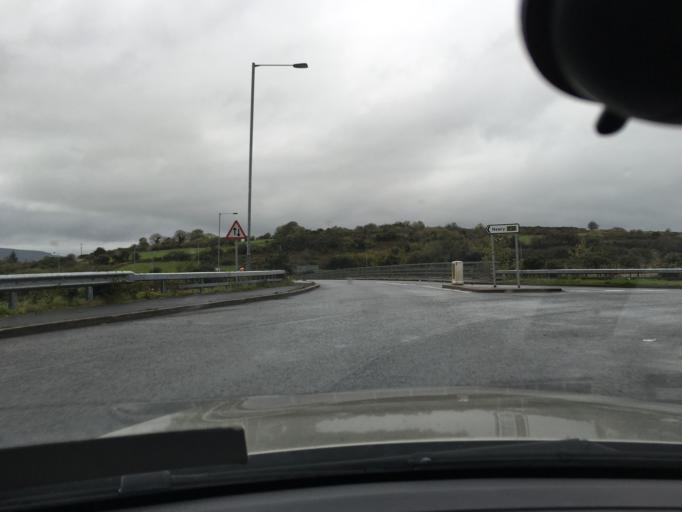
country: GB
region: Northern Ireland
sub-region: Newry and Mourne District
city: Newry
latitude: 54.1379
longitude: -6.3430
